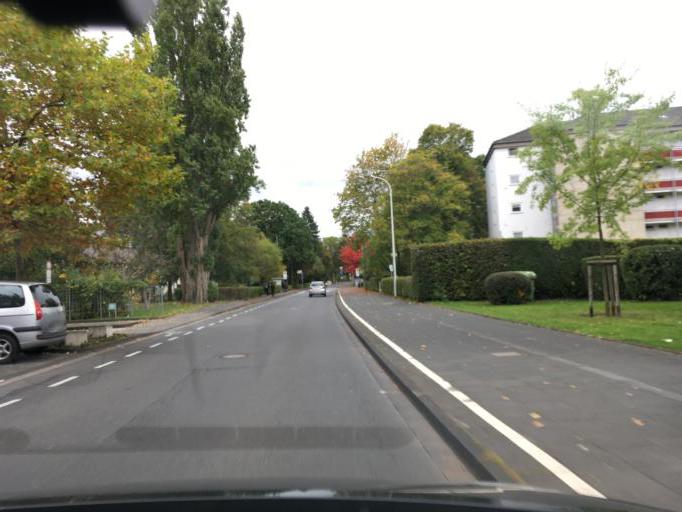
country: DE
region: North Rhine-Westphalia
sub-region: Regierungsbezirk Koln
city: Konigswinter
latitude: 50.6780
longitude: 7.1626
